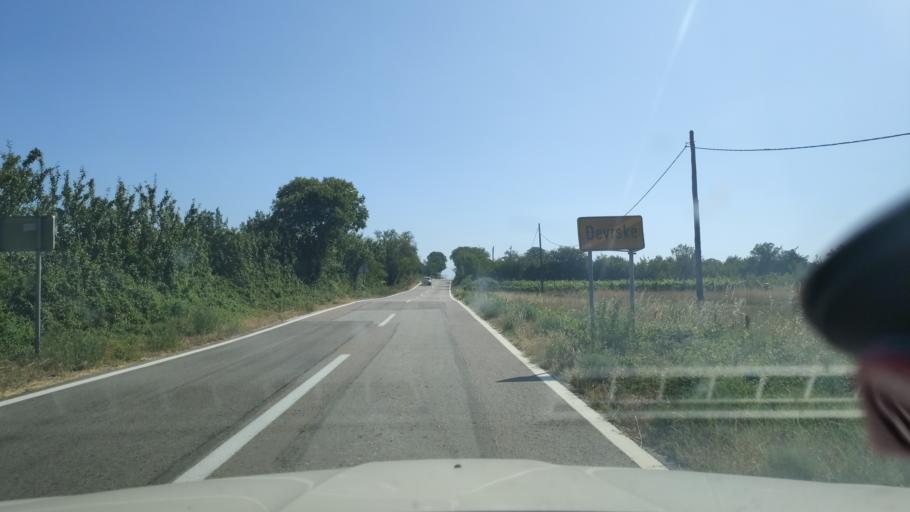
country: HR
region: Sibensko-Kniniska
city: Kistanje
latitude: 43.9560
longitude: 15.8580
